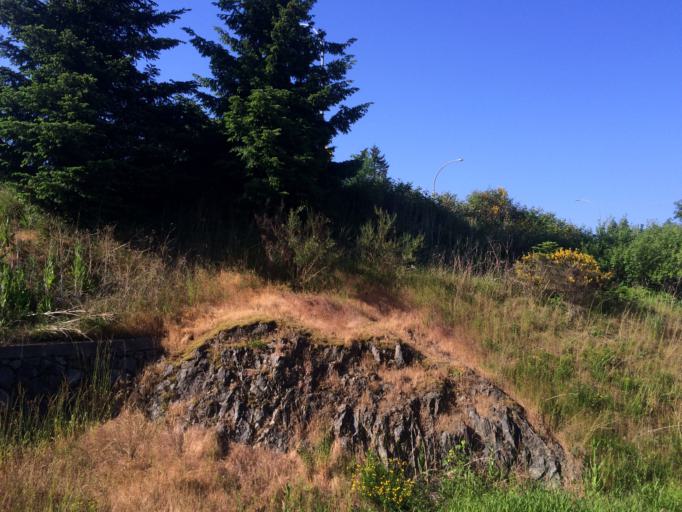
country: CA
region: British Columbia
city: Colwood
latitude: 48.4628
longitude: -123.4487
